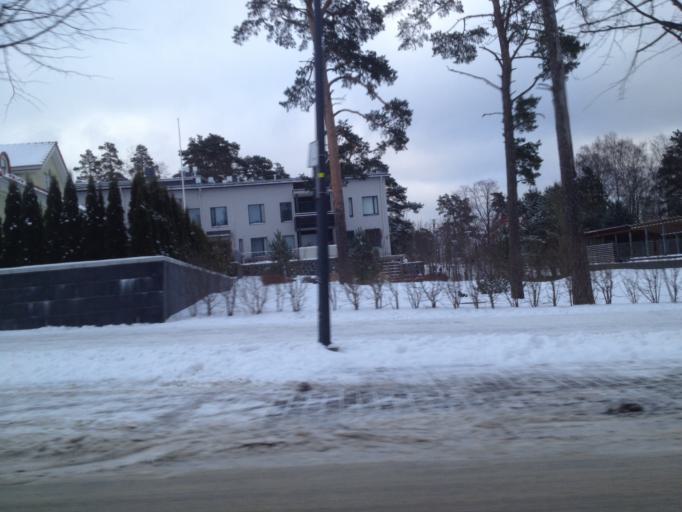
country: FI
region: Uusimaa
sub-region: Helsinki
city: Vantaa
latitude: 60.2023
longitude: 25.1498
